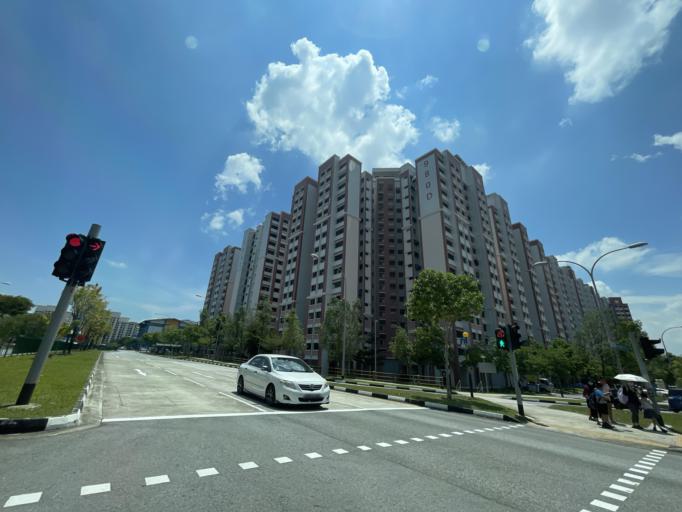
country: MY
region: Johor
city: Kampung Pasir Gudang Baru
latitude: 1.3809
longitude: 103.8815
